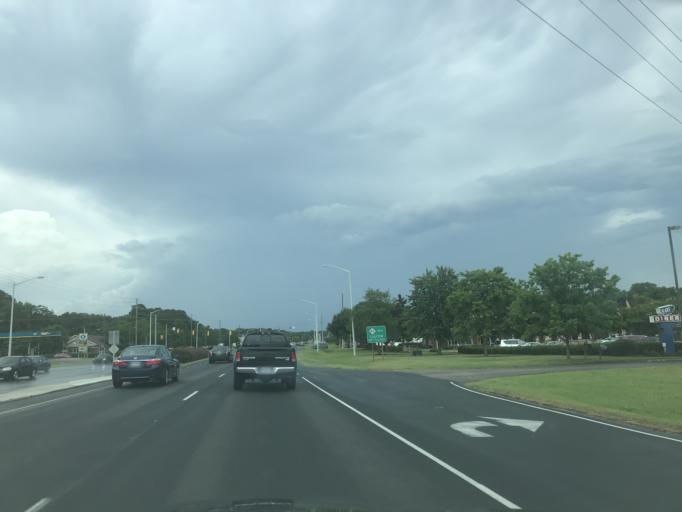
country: US
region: North Carolina
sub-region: Johnston County
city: Clayton
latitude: 35.6545
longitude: -78.4745
